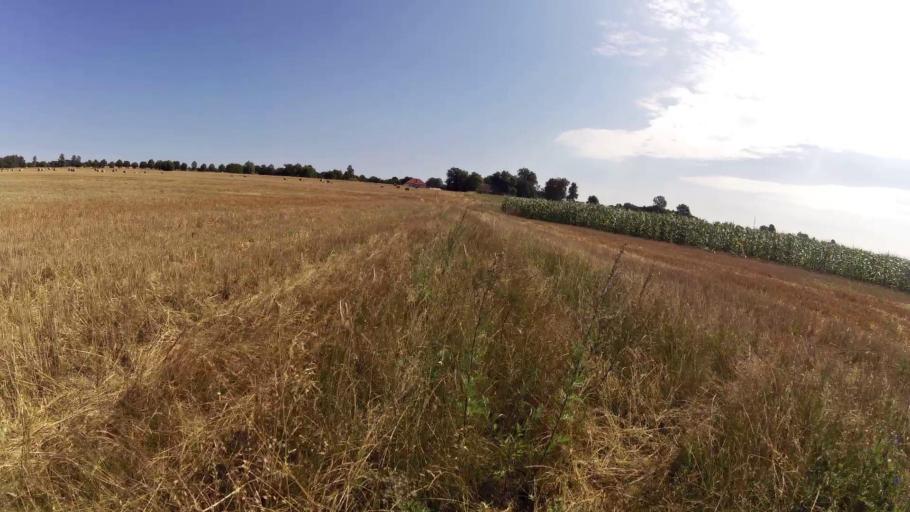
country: PL
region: West Pomeranian Voivodeship
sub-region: Powiat stargardzki
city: Dobrzany
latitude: 53.2808
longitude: 15.4523
